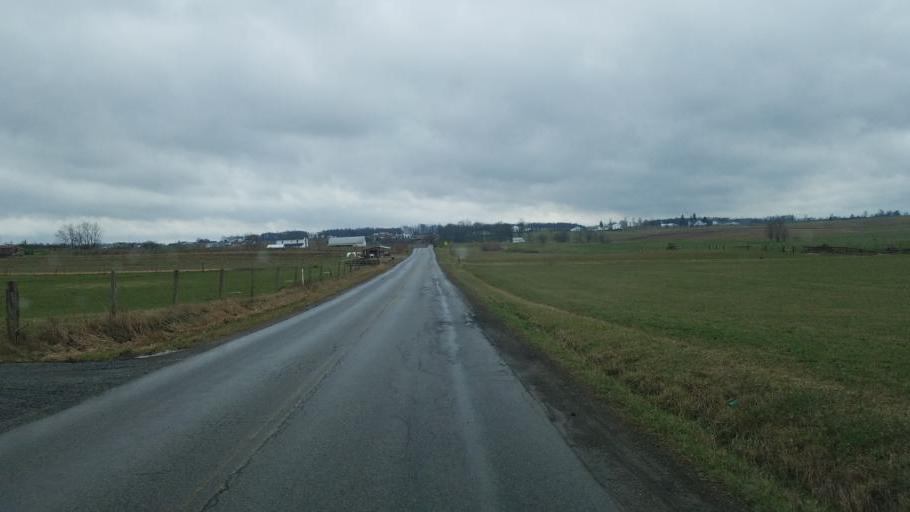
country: US
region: Ohio
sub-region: Wayne County
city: Apple Creek
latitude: 40.6873
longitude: -81.7841
